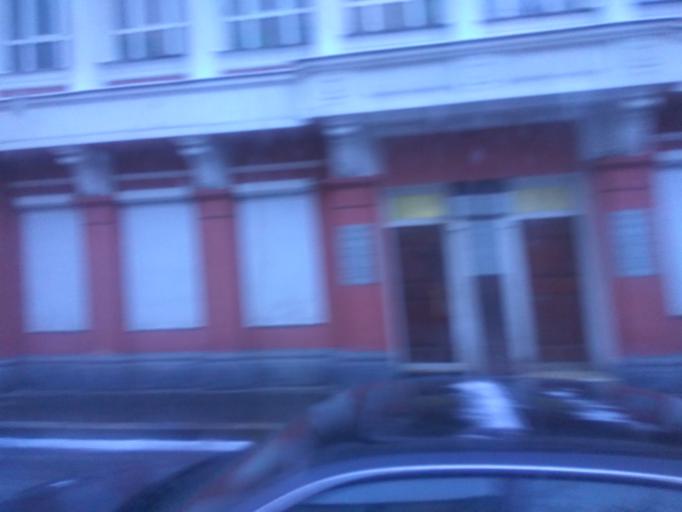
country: RU
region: Moscow
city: Taganskiy
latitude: 55.7317
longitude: 37.6798
